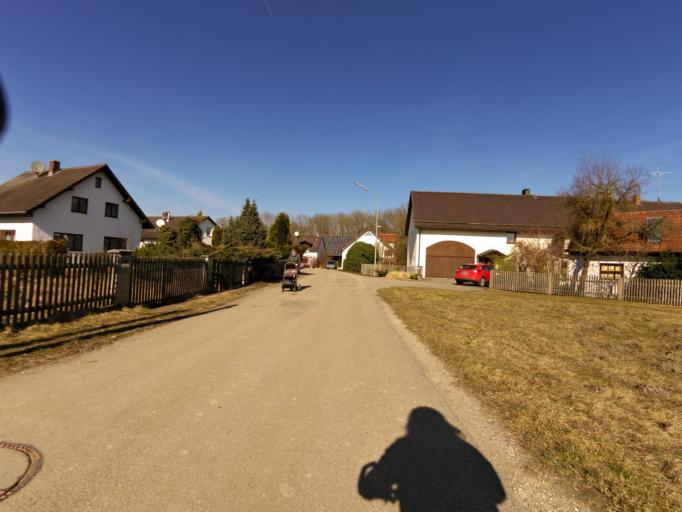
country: DE
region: Bavaria
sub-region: Upper Bavaria
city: Wang
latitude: 48.4948
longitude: 11.9663
